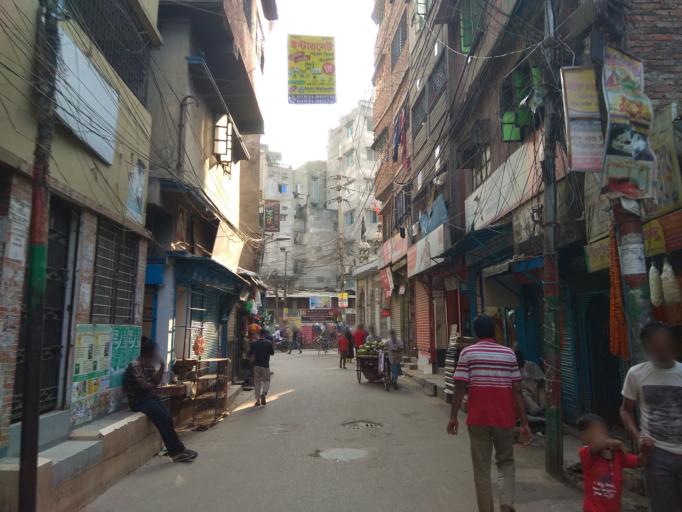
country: BD
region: Dhaka
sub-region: Dhaka
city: Dhaka
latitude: 23.7190
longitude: 90.4006
